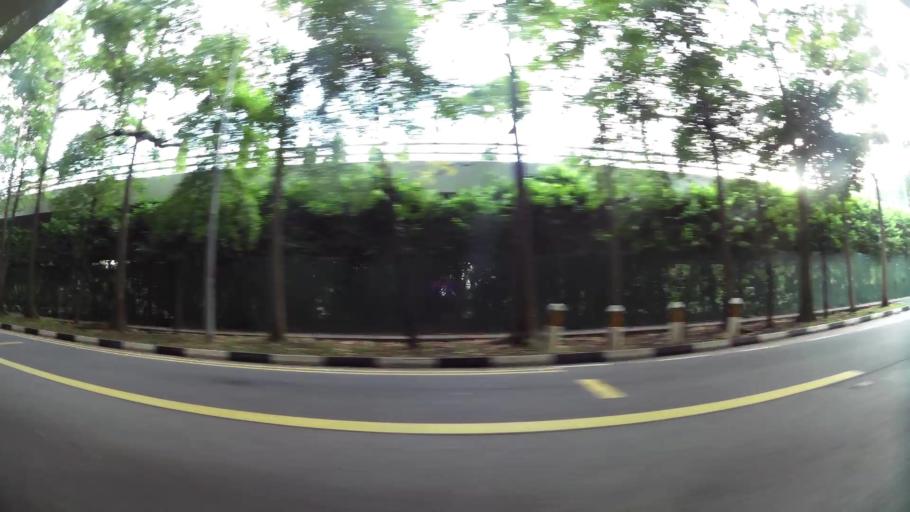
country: SG
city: Singapore
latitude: 1.2713
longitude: 103.8069
